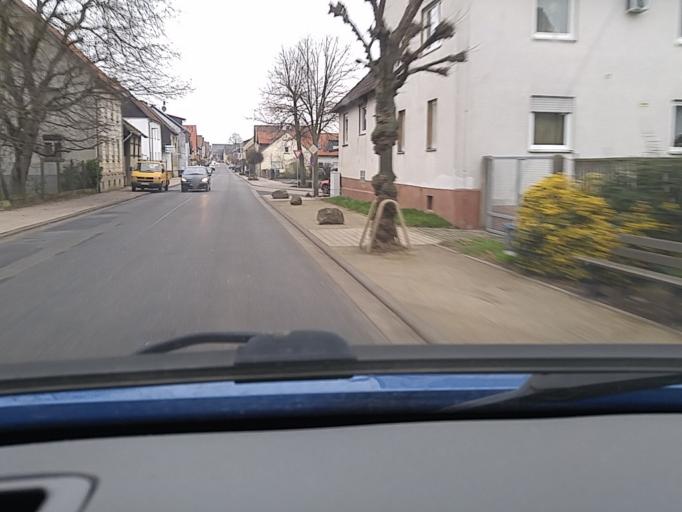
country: DE
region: Hesse
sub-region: Regierungsbezirk Darmstadt
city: Echzell
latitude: 50.3846
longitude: 8.8831
